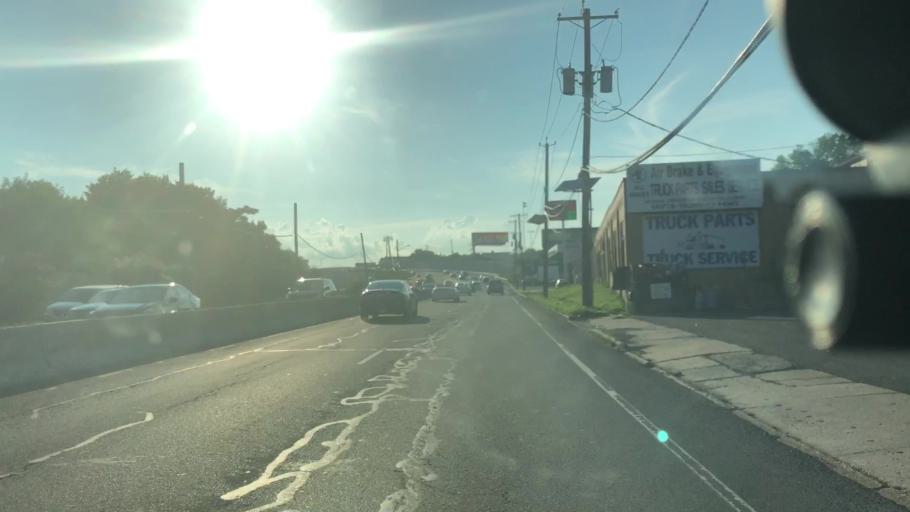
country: US
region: New Jersey
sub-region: Union County
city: Hillside
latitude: 40.6980
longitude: -74.2256
